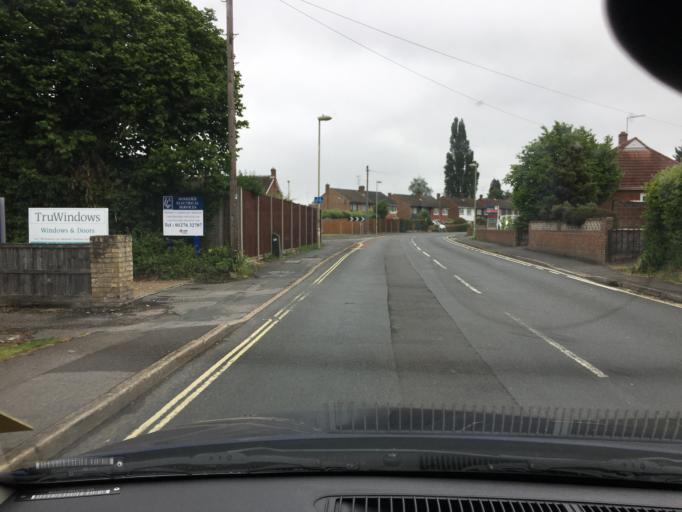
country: GB
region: England
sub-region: Bracknell Forest
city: Sandhurst
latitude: 51.3328
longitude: -0.7825
